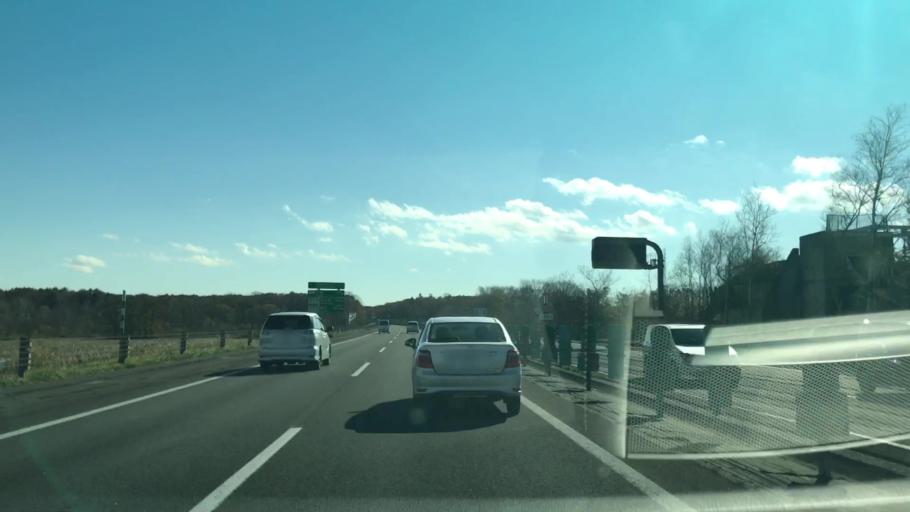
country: JP
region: Hokkaido
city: Chitose
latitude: 42.8662
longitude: 141.5568
